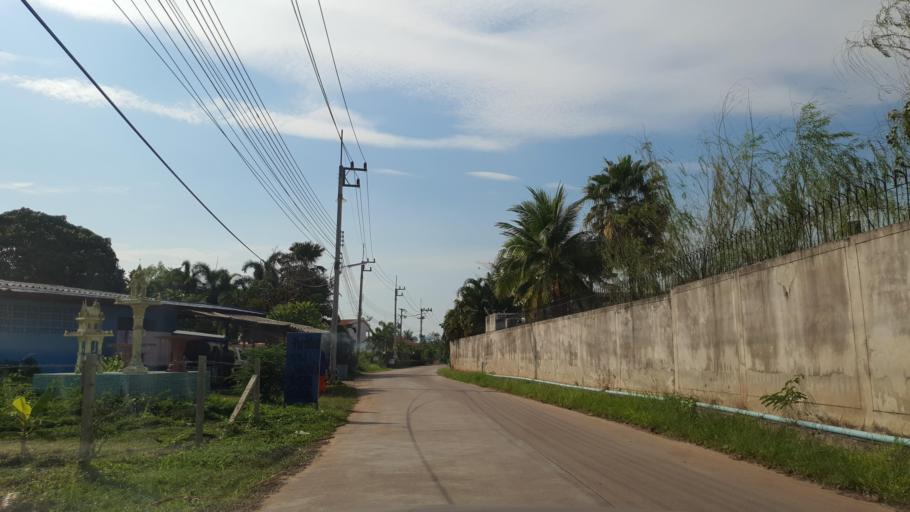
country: TH
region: Chon Buri
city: Phatthaya
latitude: 12.8028
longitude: 100.9330
